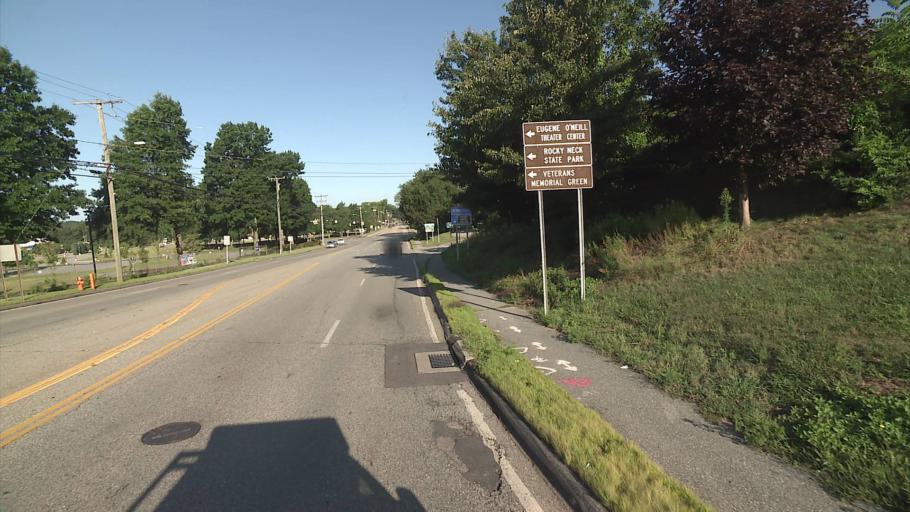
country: US
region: Connecticut
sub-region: New London County
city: Central Waterford
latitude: 41.3424
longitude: -72.1276
